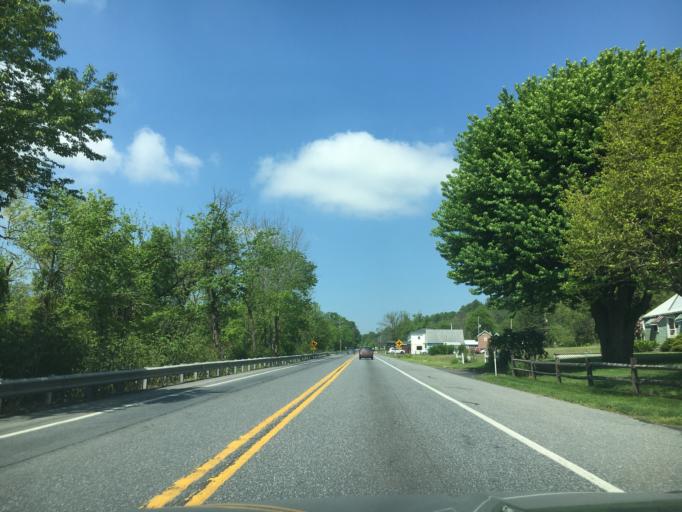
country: US
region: Pennsylvania
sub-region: Berks County
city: New Berlinville
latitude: 40.3623
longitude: -75.6721
